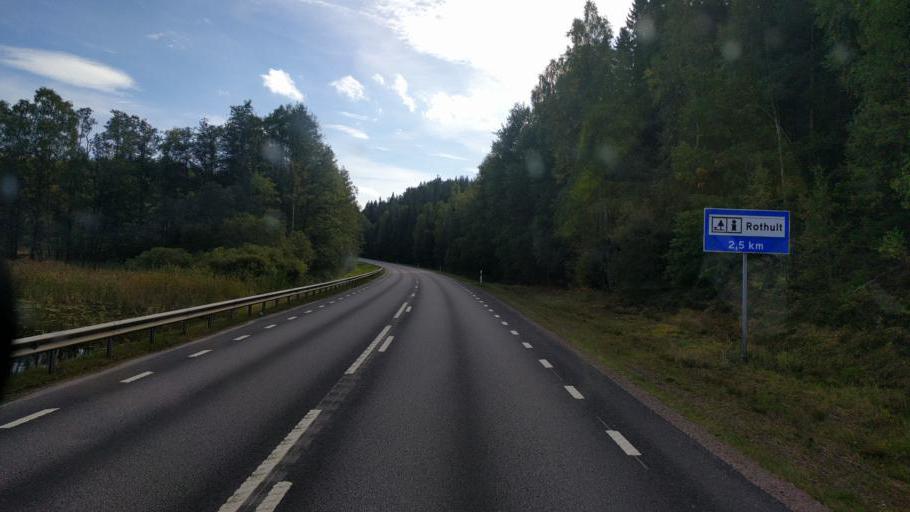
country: SE
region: OEstergoetland
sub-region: Kinda Kommun
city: Kisa
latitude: 57.9561
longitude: 15.6603
